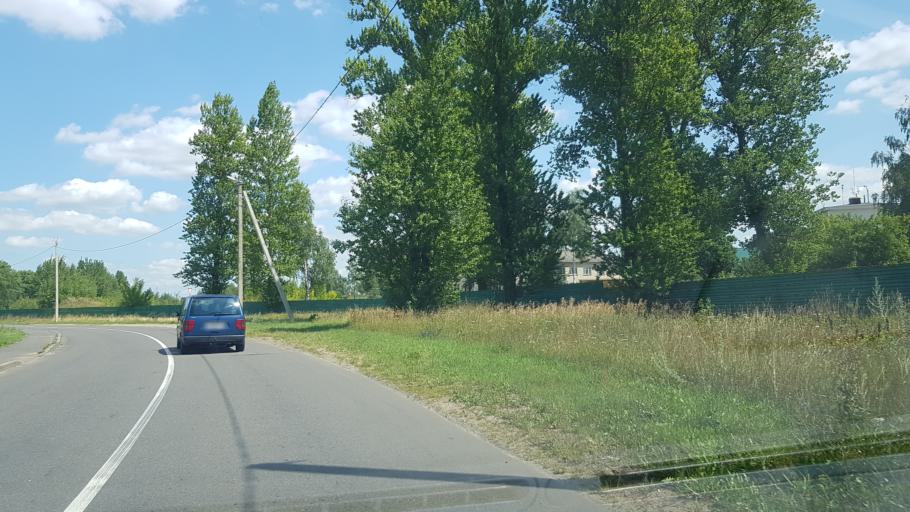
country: BY
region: Mogilev
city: Babruysk
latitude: 53.1082
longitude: 29.1978
